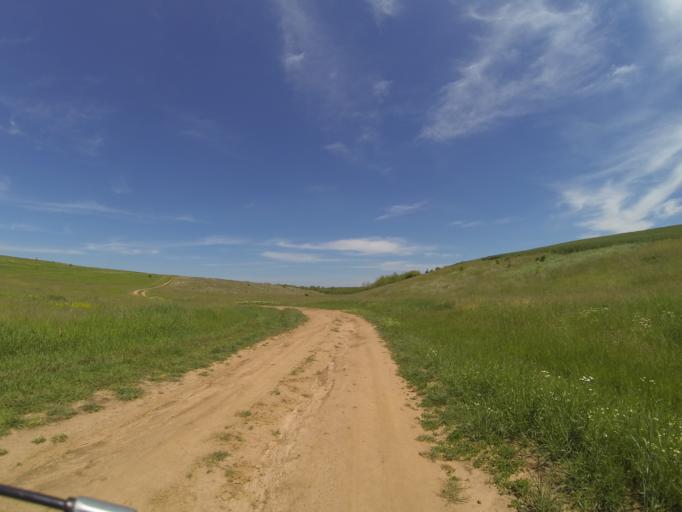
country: RO
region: Dolj
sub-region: Comuna Teslui
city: Teslui
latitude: 44.1775
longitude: 24.1687
